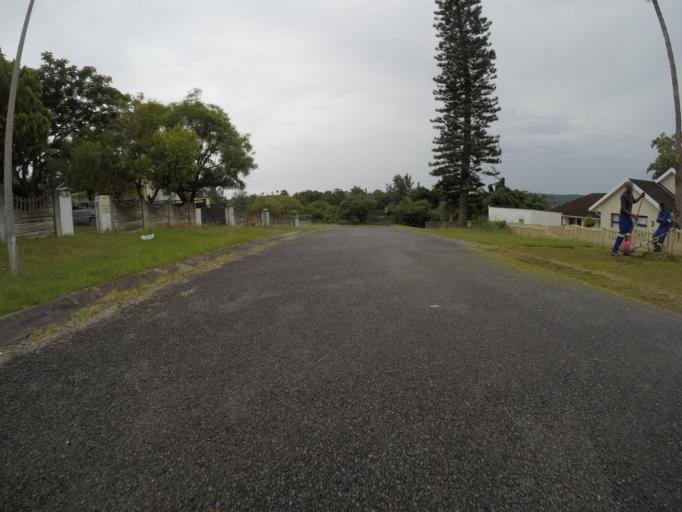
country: ZA
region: Eastern Cape
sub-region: Buffalo City Metropolitan Municipality
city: East London
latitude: -32.9647
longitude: 27.8481
